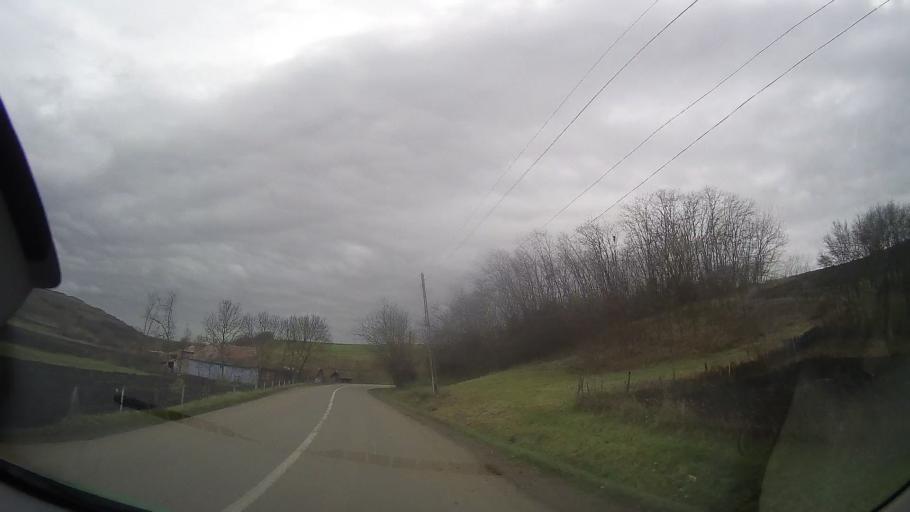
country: RO
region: Mures
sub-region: Comuna Craesti
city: Craiesti
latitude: 46.7727
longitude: 24.4249
